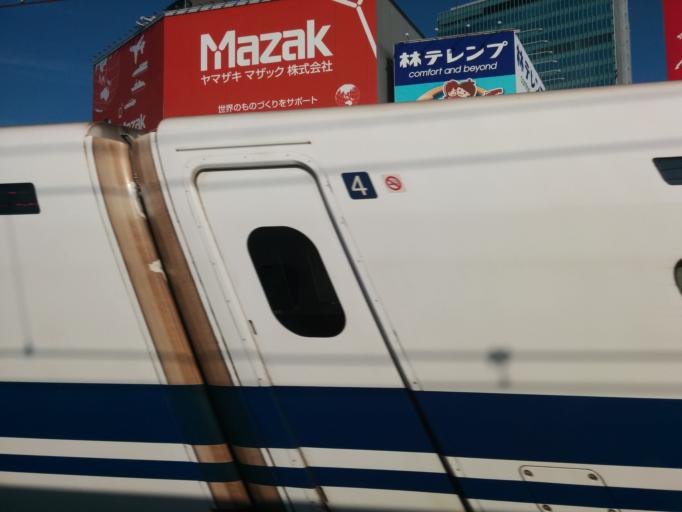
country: JP
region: Aichi
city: Nagoya-shi
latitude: 35.1650
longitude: 136.8846
